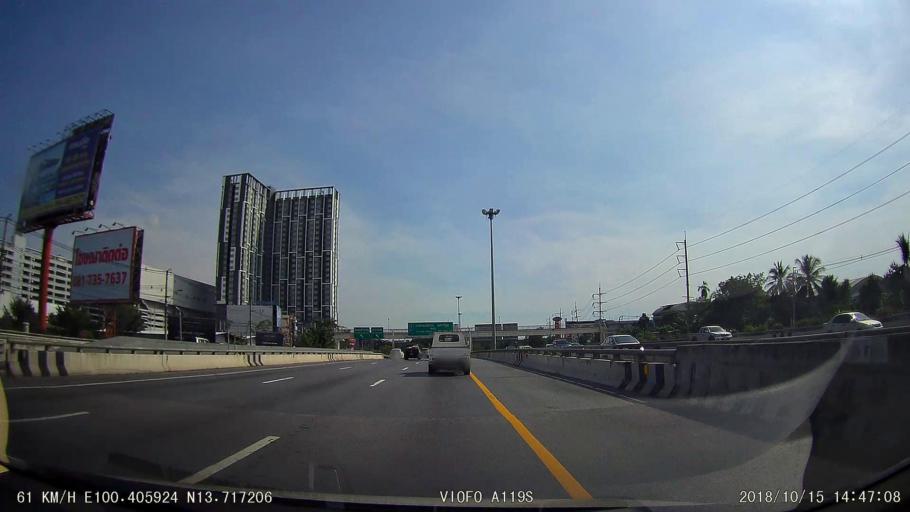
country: TH
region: Bangkok
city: Bang Khae
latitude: 13.7169
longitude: 100.4059
